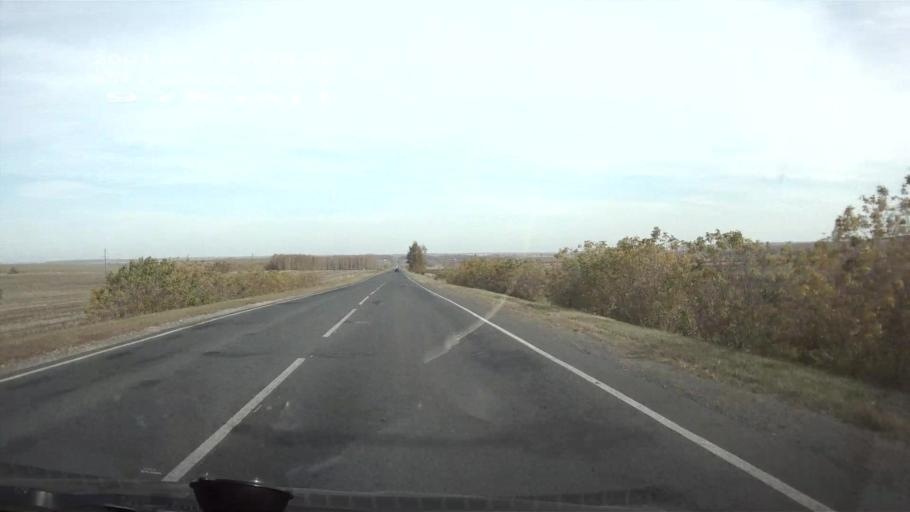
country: RU
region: Mordoviya
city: Atyashevo
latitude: 54.5391
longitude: 45.9318
